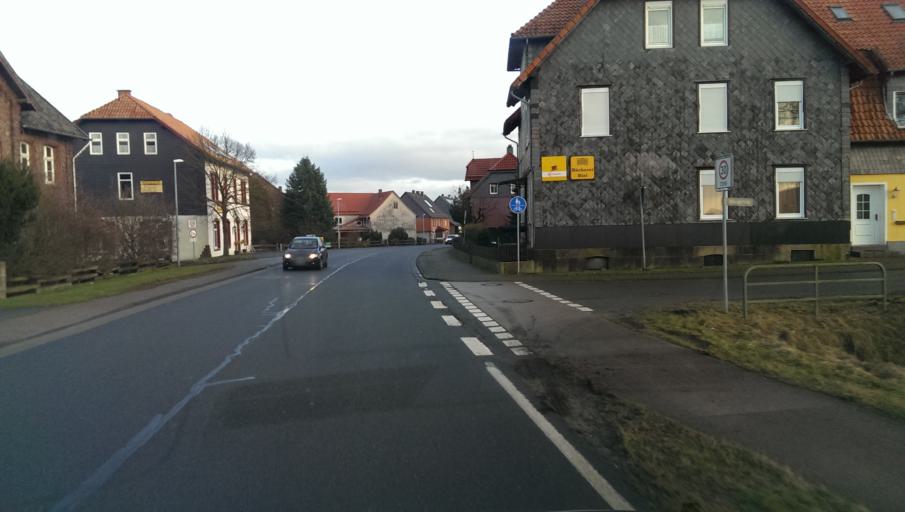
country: DE
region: Lower Saxony
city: Eimen
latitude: 51.8870
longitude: 9.7474
